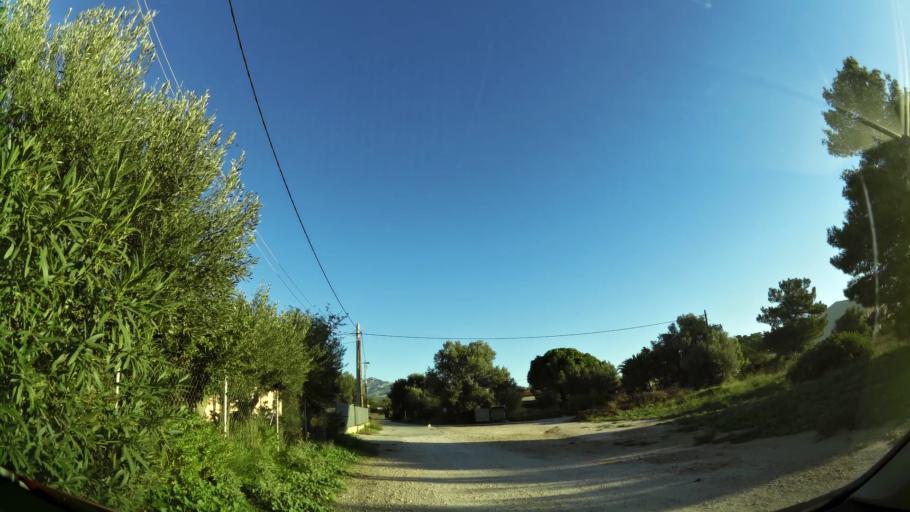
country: GR
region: Attica
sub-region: Nomarchia Anatolikis Attikis
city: Pallini
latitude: 37.9994
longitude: 23.8682
